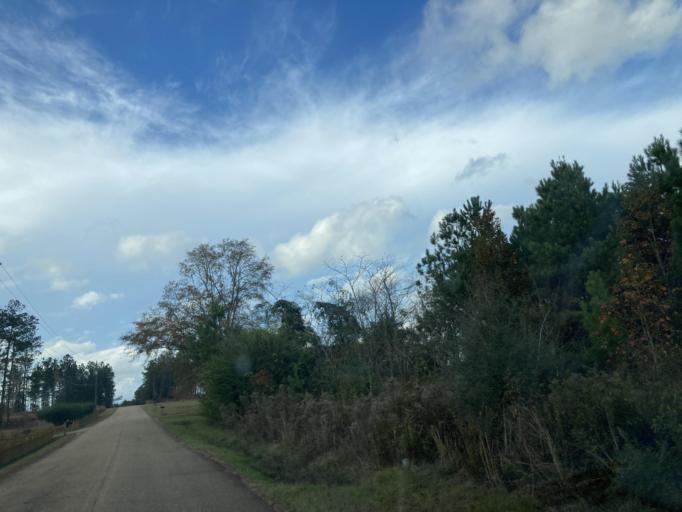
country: US
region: Mississippi
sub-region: Lamar County
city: Purvis
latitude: 31.1352
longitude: -89.6187
